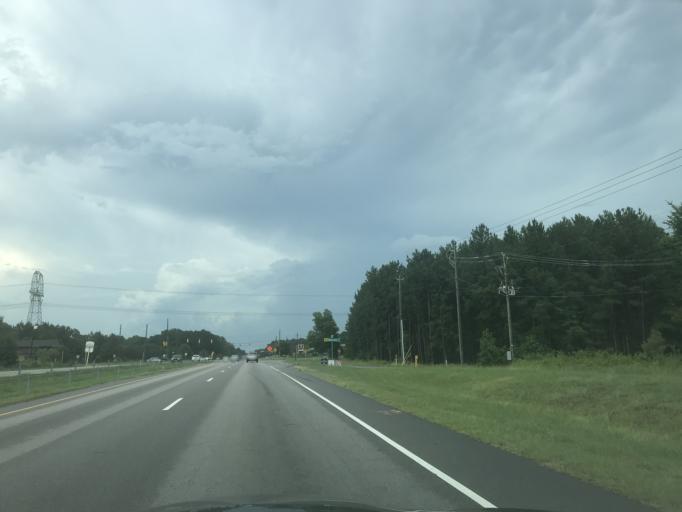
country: US
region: North Carolina
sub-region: Johnston County
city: Clayton
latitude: 35.6772
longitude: -78.5233
